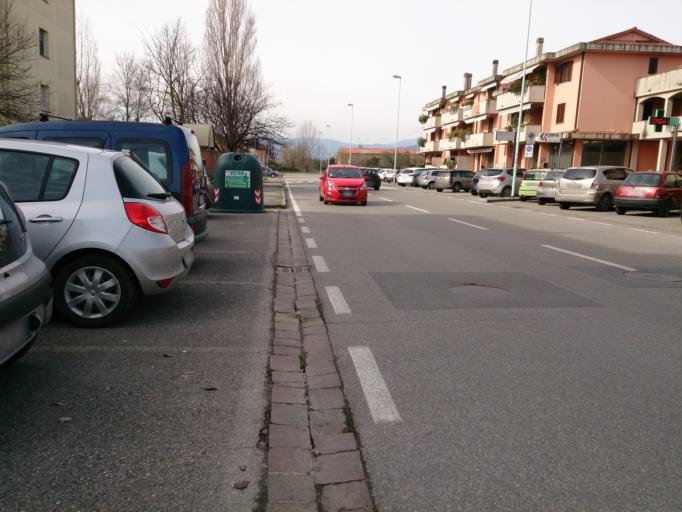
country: IT
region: Tuscany
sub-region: Provincia di Prato
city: Fornacelle
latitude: 43.8901
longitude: 11.0454
